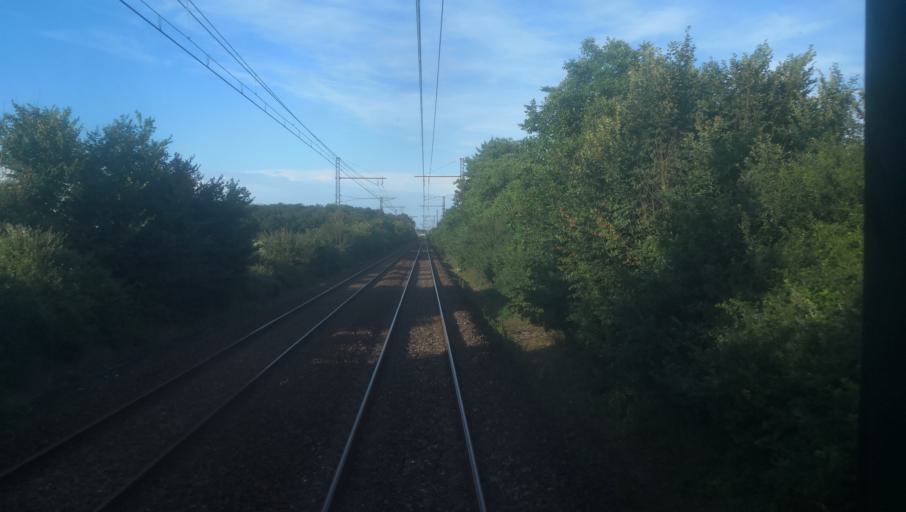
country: FR
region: Centre
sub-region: Departement de l'Indre
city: Neuvy-Pailloux
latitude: 46.8654
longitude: 1.8295
